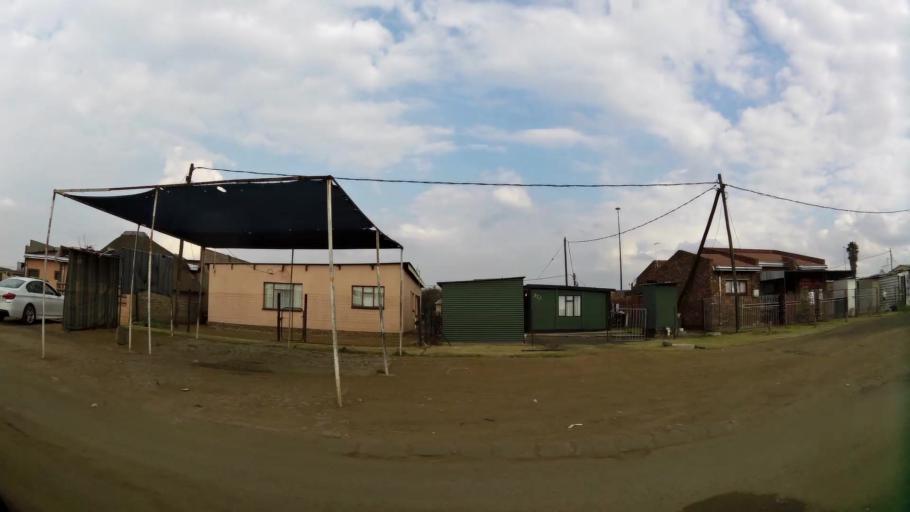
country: ZA
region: Gauteng
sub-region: Sedibeng District Municipality
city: Vanderbijlpark
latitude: -26.6750
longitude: 27.8716
